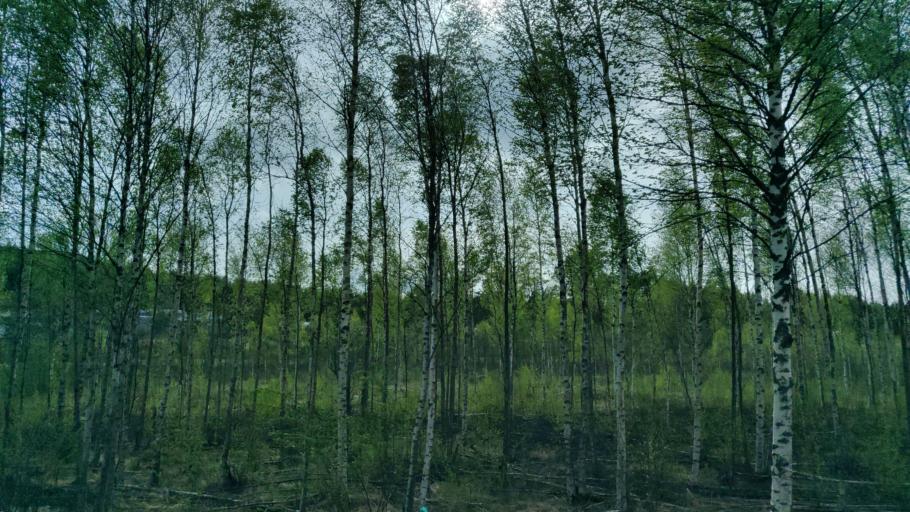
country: SE
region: Vaermland
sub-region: Forshaga Kommun
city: Deje
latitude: 59.6208
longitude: 13.4465
